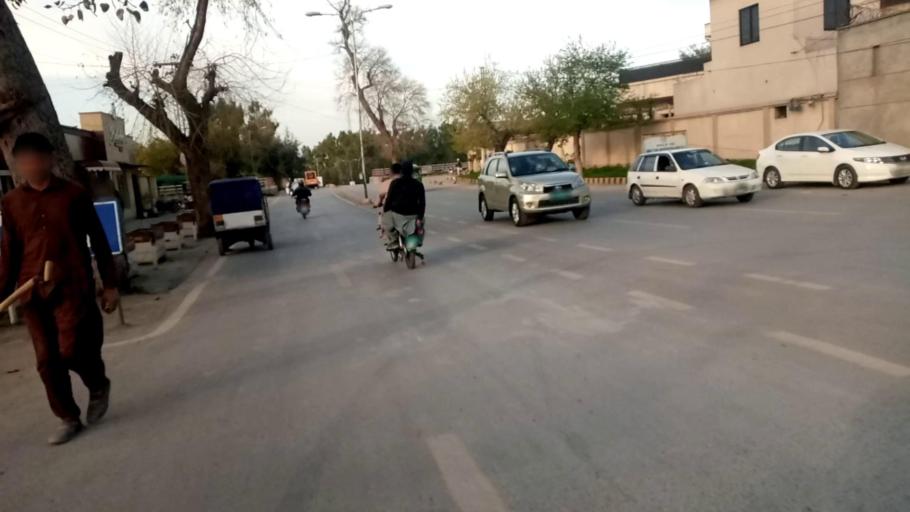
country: PK
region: Khyber Pakhtunkhwa
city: Peshawar
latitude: 34.0151
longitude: 71.5521
